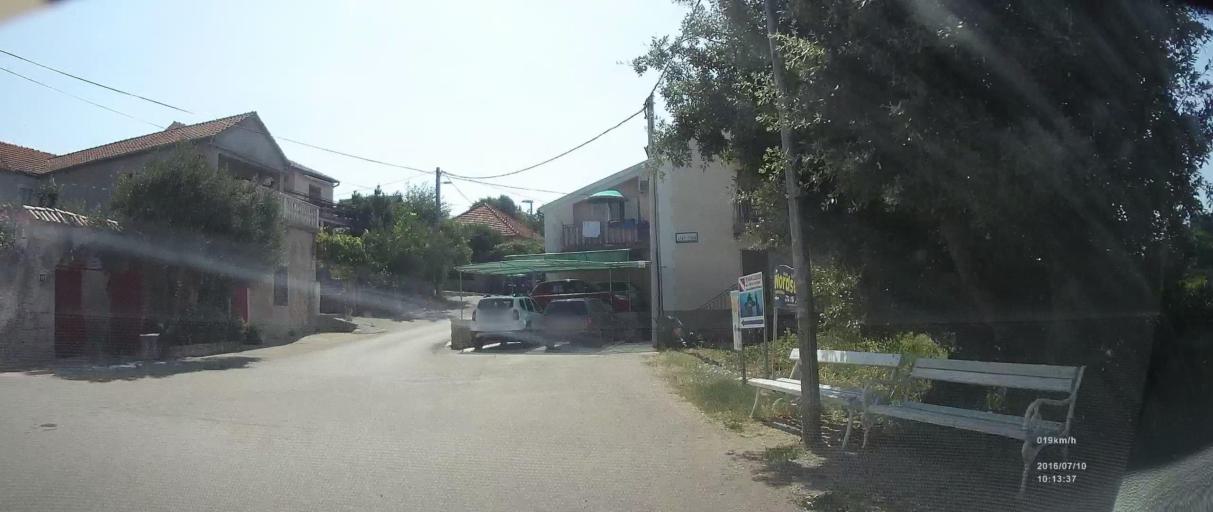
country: HR
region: Zadarska
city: Pakostane
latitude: 43.9082
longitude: 15.5147
